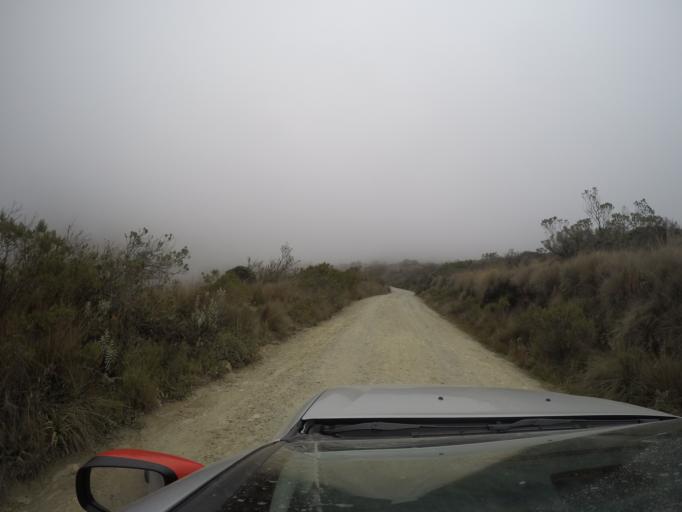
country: CO
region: Tolima
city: Murillo
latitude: 4.9352
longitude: -75.3498
